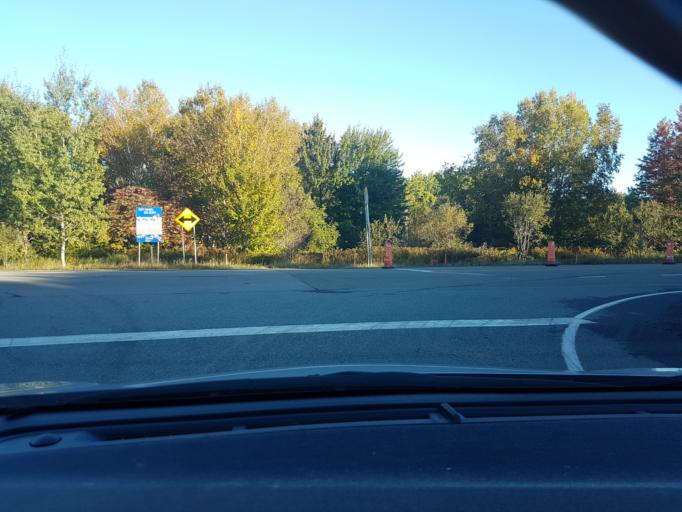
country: CA
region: Quebec
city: L'Ancienne-Lorette
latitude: 46.7874
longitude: -71.3278
